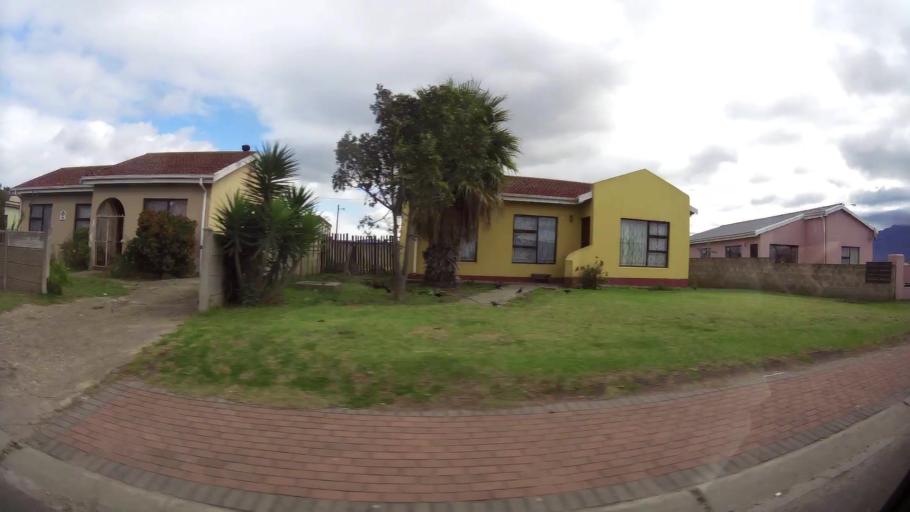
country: ZA
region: Western Cape
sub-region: Eden District Municipality
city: George
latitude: -34.0175
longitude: 22.4696
